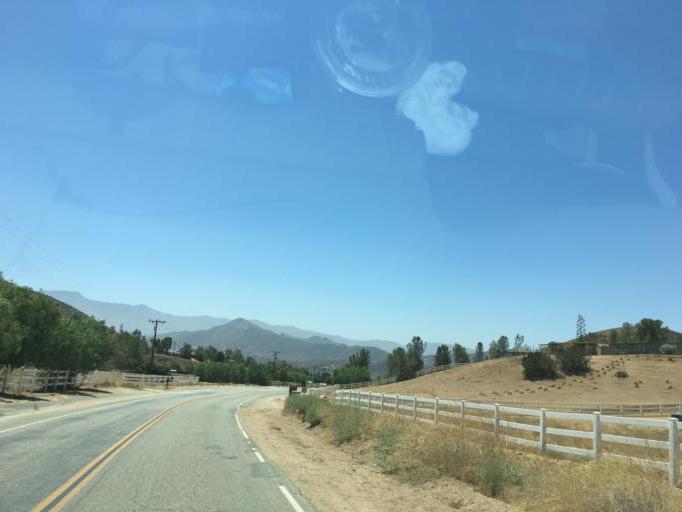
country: US
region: California
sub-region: Los Angeles County
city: Acton
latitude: 34.5095
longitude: -118.2160
